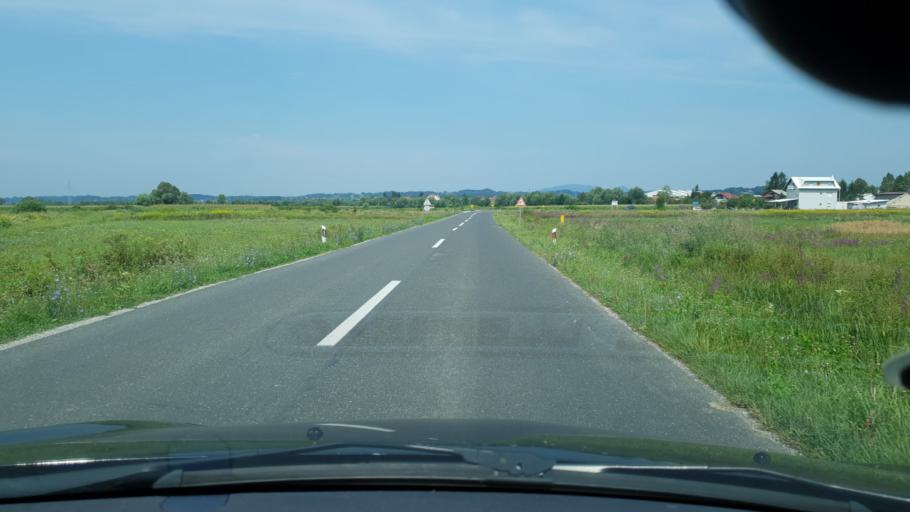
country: HR
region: Krapinsko-Zagorska
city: Marija Bistrica
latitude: 46.0398
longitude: 16.0839
